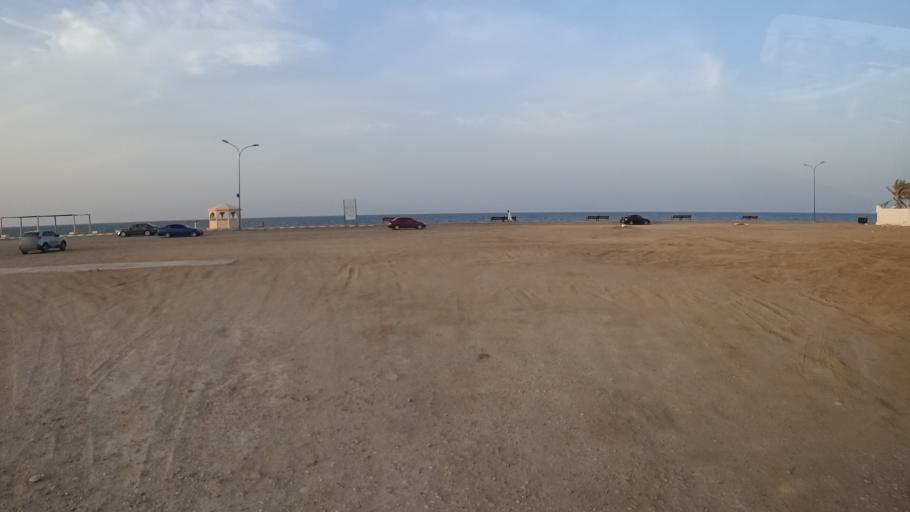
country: OM
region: Ash Sharqiyah
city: Sur
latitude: 22.5936
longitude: 59.4969
